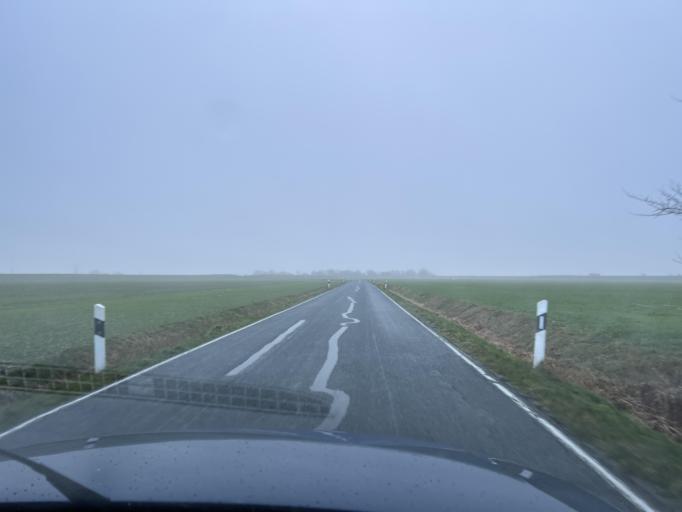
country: DE
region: Schleswig-Holstein
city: Strubbel
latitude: 54.2708
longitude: 8.9445
